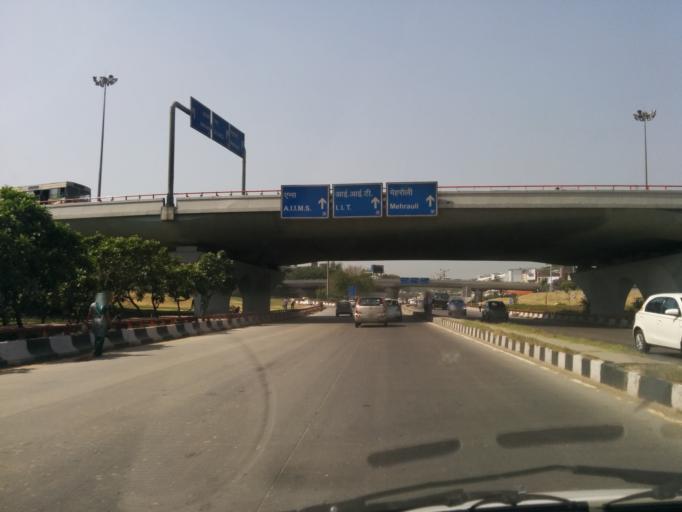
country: IN
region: NCT
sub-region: New Delhi
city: New Delhi
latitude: 28.5711
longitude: 77.2091
